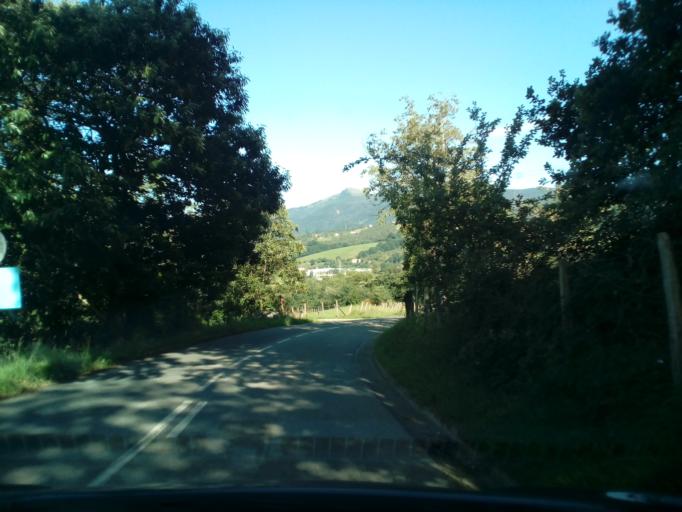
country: ES
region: Basque Country
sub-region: Provincia de Guipuzcoa
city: Aduna
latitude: 43.2056
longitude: -2.0495
